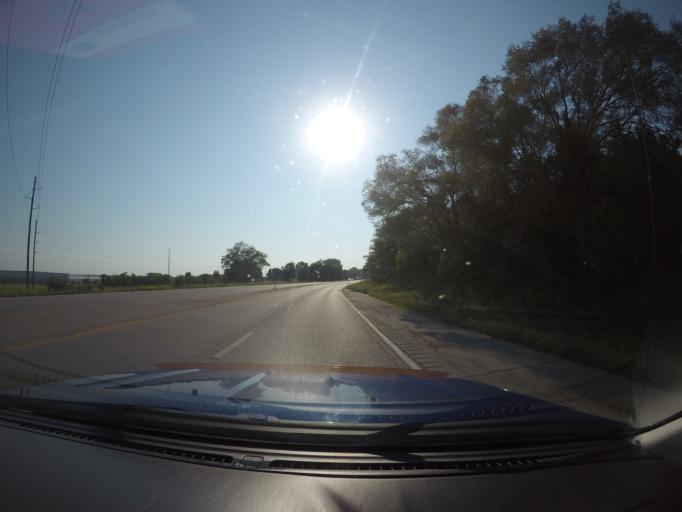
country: US
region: Kansas
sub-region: Wyandotte County
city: Edwardsville
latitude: 39.0610
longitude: -94.7997
